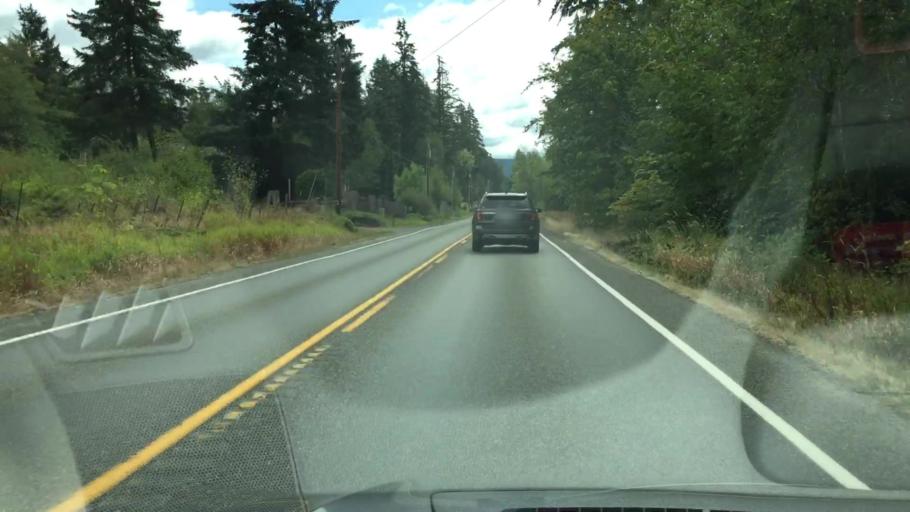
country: US
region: Washington
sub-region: Pierce County
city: Eatonville
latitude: 46.9006
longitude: -122.2977
